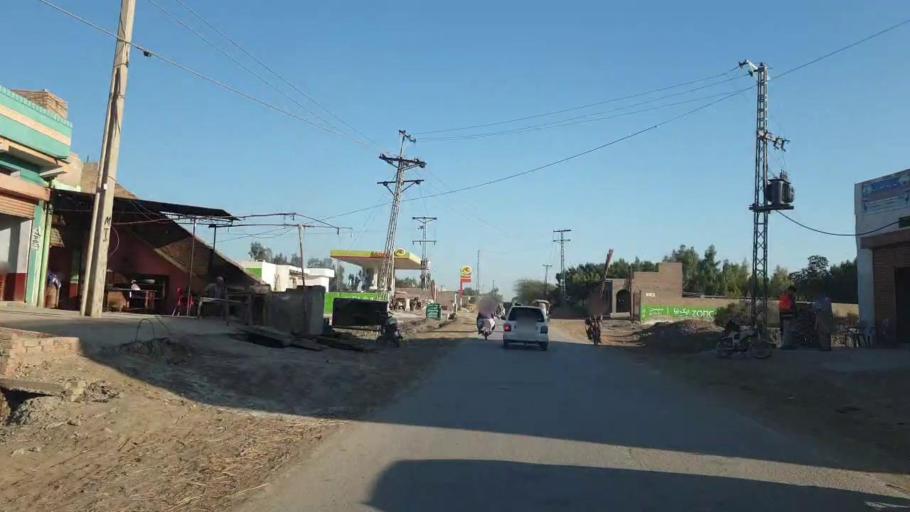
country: PK
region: Sindh
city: Dokri
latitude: 27.3682
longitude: 68.1092
